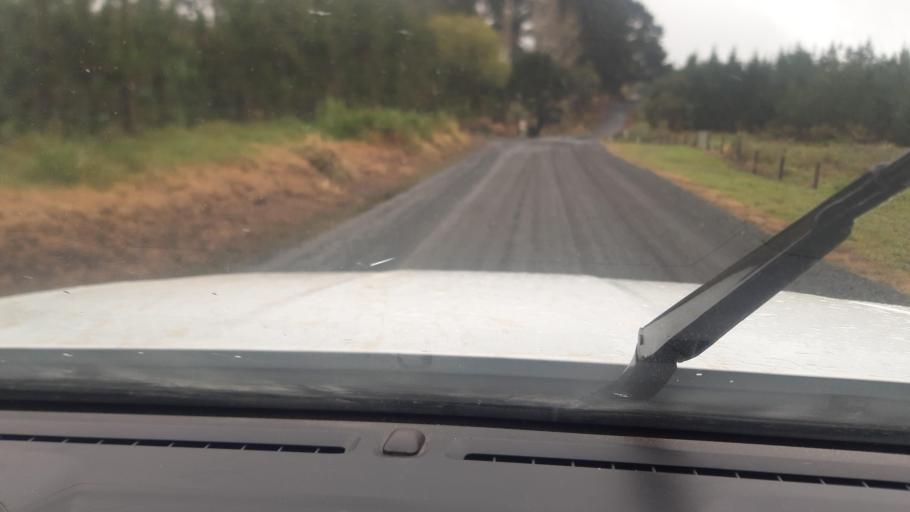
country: NZ
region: Northland
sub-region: Far North District
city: Kaitaia
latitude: -34.9740
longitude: 173.2057
